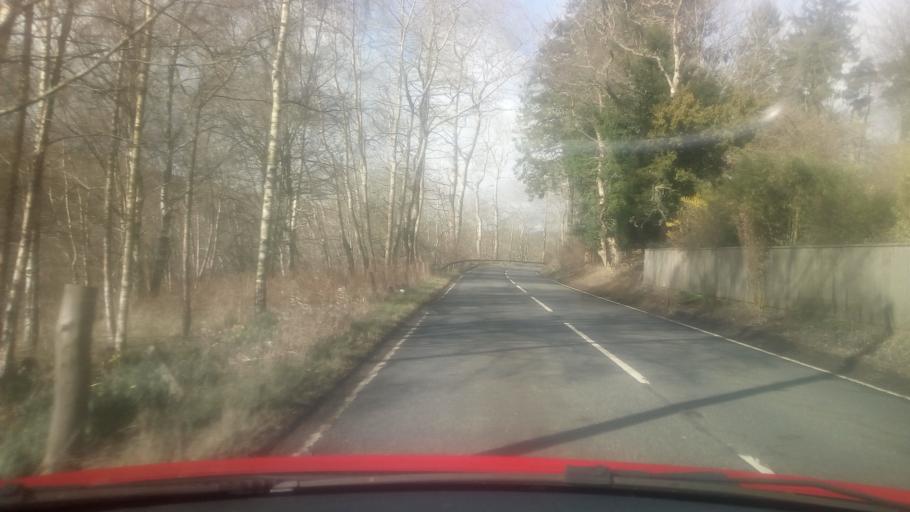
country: GB
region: Scotland
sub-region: The Scottish Borders
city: Selkirk
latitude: 55.6090
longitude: -2.9043
